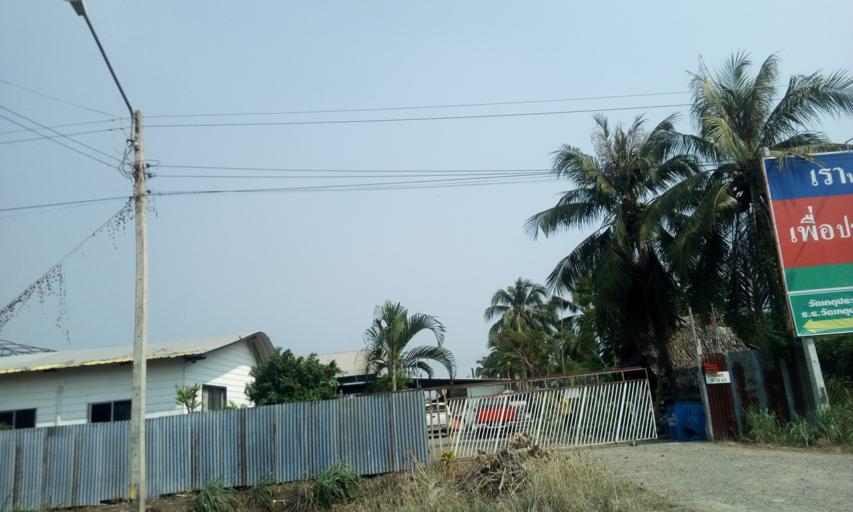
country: TH
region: Pathum Thani
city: Lam Luk Ka
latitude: 13.9614
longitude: 100.7254
